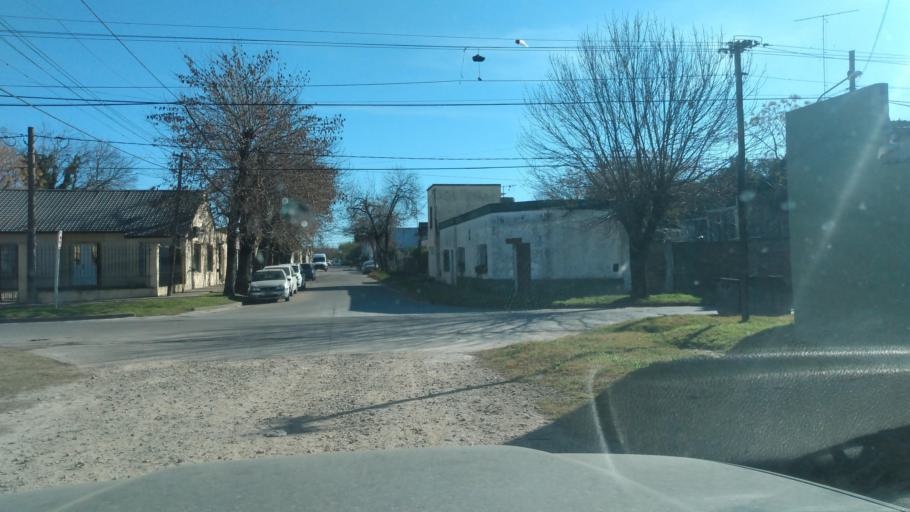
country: AR
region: Buenos Aires
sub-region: Partido de Lujan
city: Lujan
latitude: -34.5690
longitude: -59.1287
